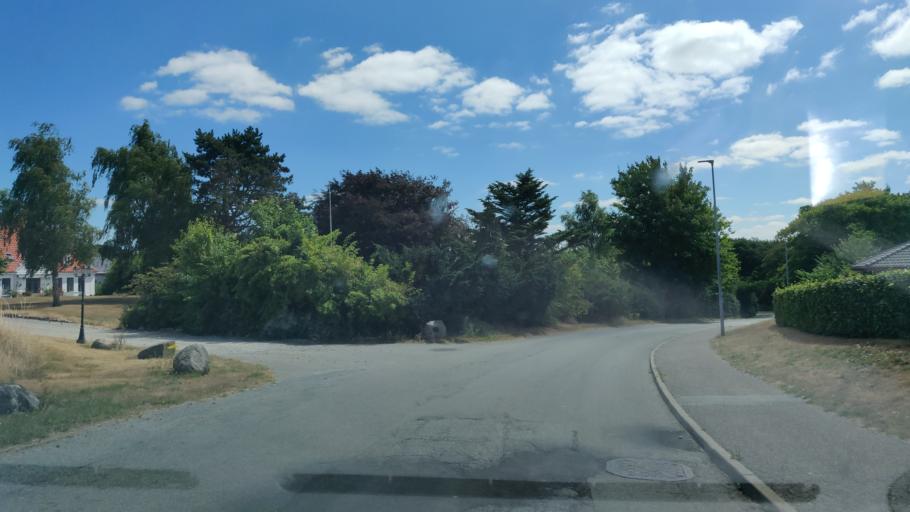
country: DK
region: South Denmark
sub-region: Kolding Kommune
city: Kolding
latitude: 55.5302
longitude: 9.5359
